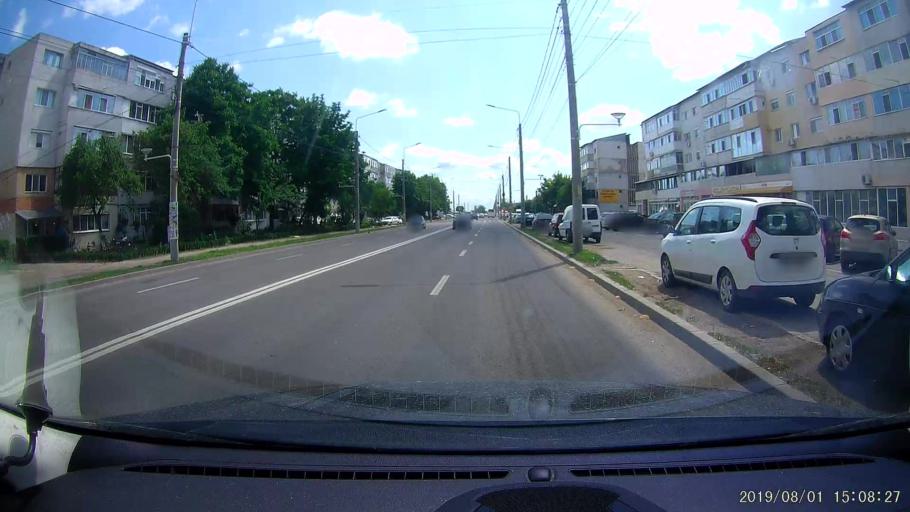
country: RO
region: Braila
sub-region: Municipiul Braila
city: Braila
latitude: 45.2414
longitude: 27.9453
